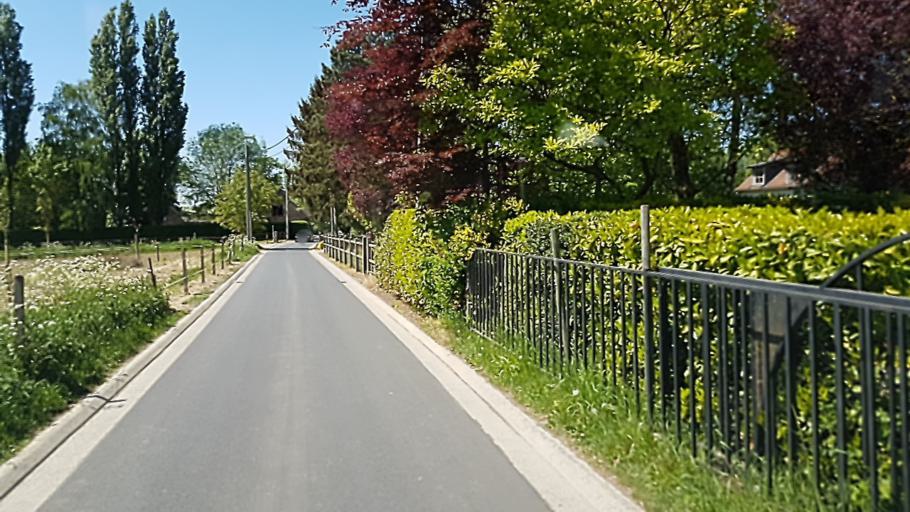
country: BE
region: Flanders
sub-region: Provincie Vlaams-Brabant
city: Ternat
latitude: 50.8993
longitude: 4.1539
